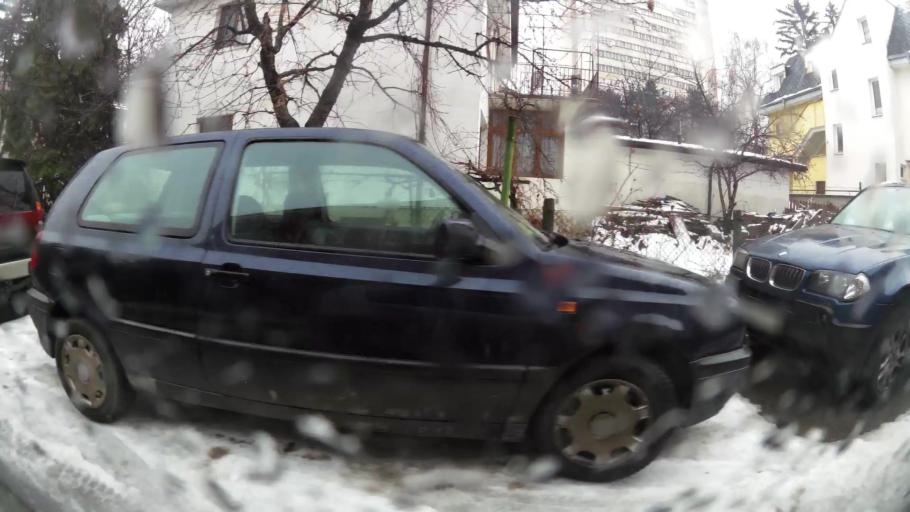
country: BG
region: Sofia-Capital
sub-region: Stolichna Obshtina
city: Sofia
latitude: 42.6636
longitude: 23.2754
